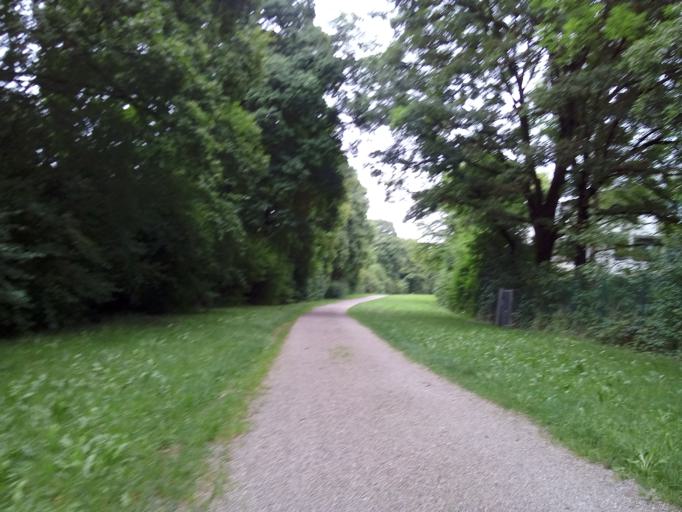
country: DE
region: Bavaria
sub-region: Upper Bavaria
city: Bogenhausen
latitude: 48.1755
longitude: 11.6060
